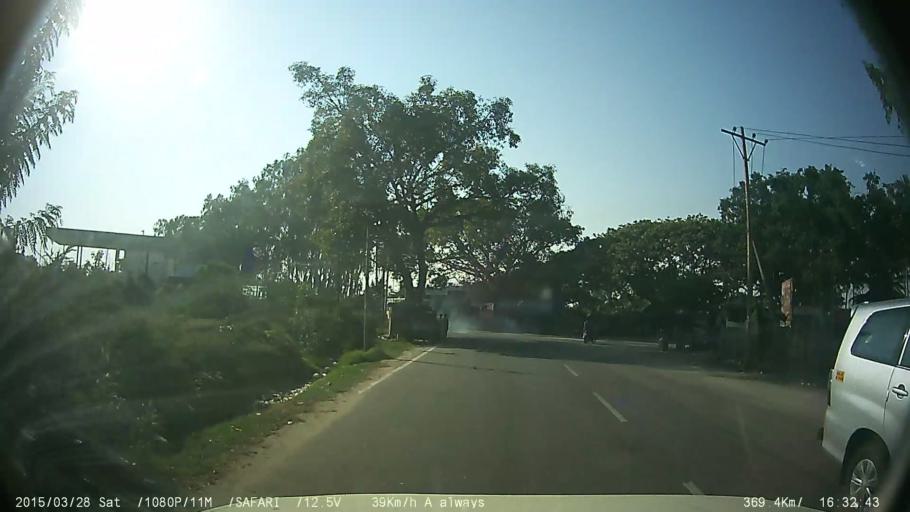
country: IN
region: Karnataka
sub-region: Mandya
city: Shrirangapattana
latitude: 12.3918
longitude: 76.6273
